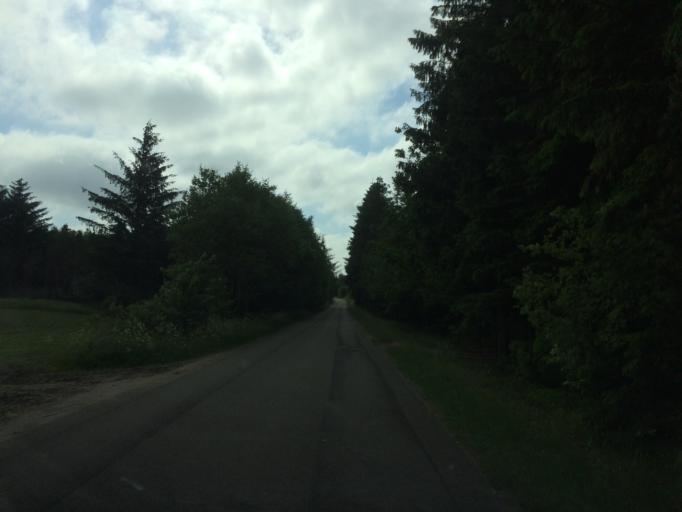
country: DK
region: Central Jutland
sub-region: Holstebro Kommune
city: Ulfborg
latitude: 56.2373
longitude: 8.4206
